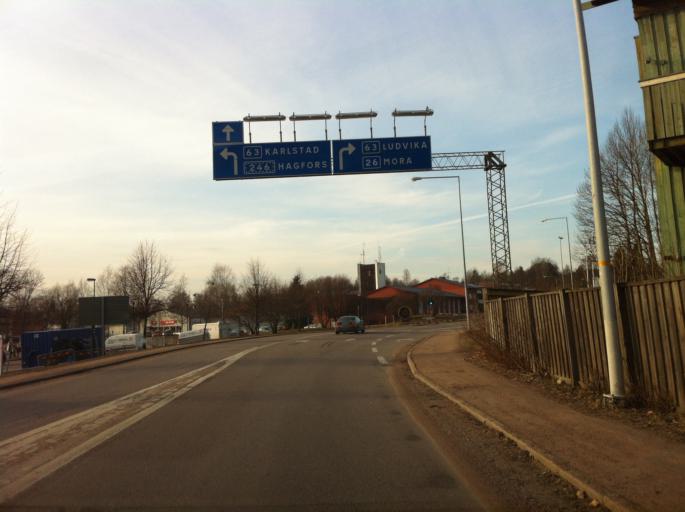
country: SE
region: Vaermland
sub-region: Filipstads Kommun
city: Filipstad
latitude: 59.7134
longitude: 14.1748
